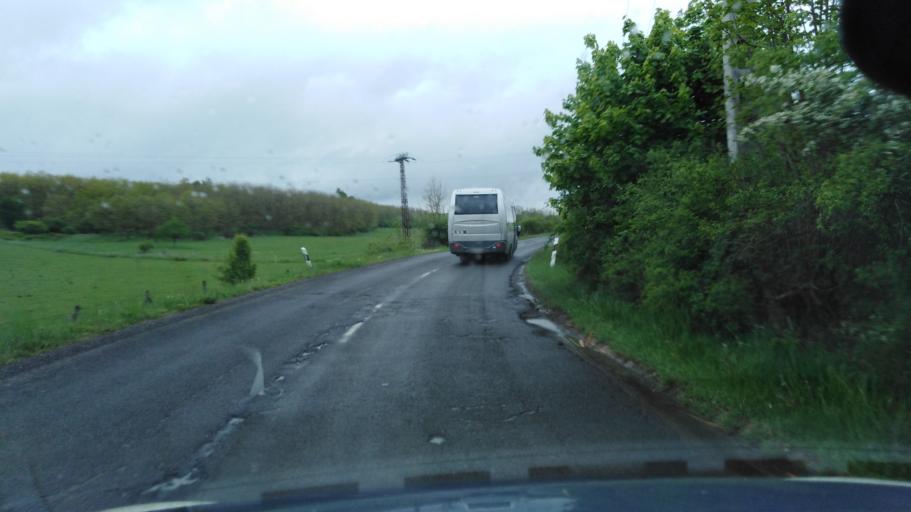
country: HU
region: Nograd
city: Rimoc
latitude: 48.0116
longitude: 19.6004
